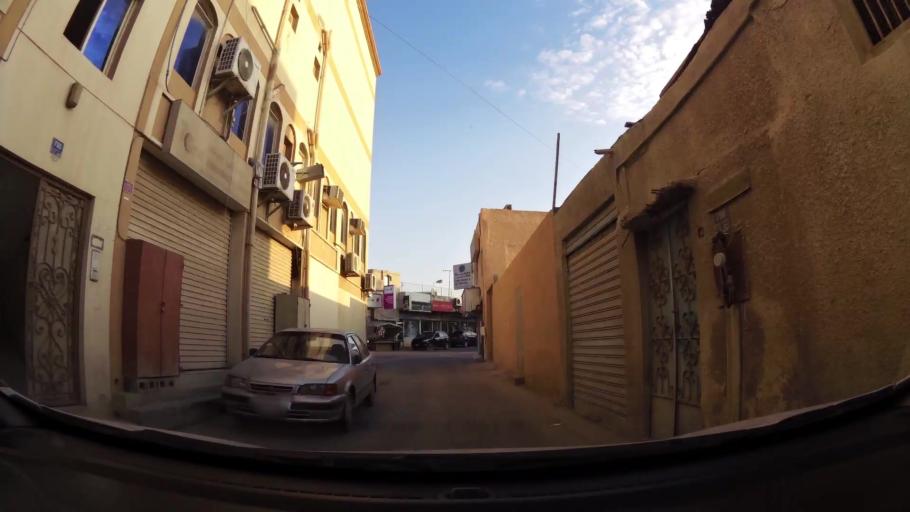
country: BH
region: Manama
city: Jidd Hafs
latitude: 26.2229
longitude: 50.5426
